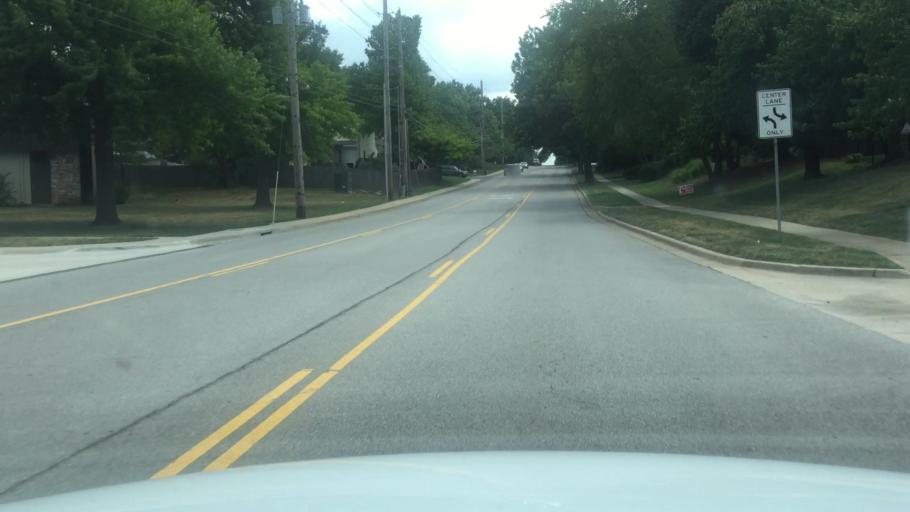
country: US
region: Kansas
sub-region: Johnson County
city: Lenexa
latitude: 38.9689
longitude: -94.7610
